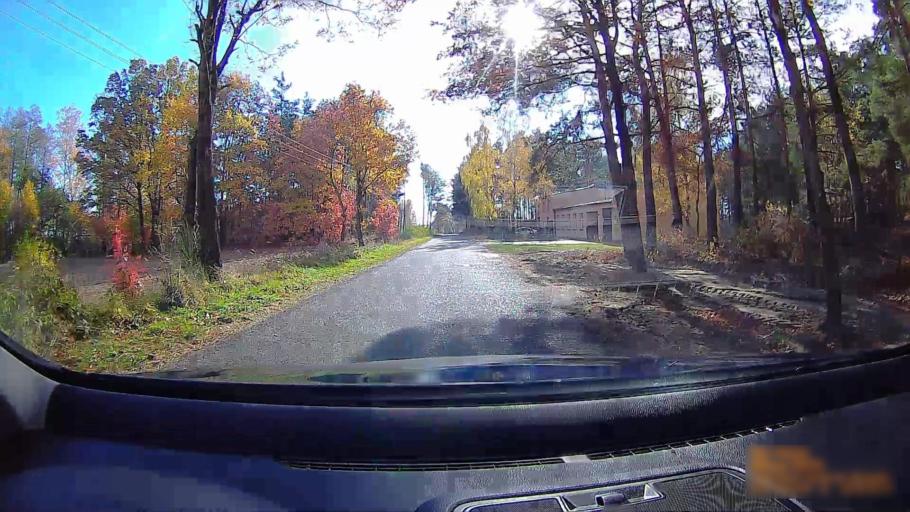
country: PL
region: Greater Poland Voivodeship
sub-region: Powiat ostrzeszowski
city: Doruchow
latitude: 51.4038
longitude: 18.0271
